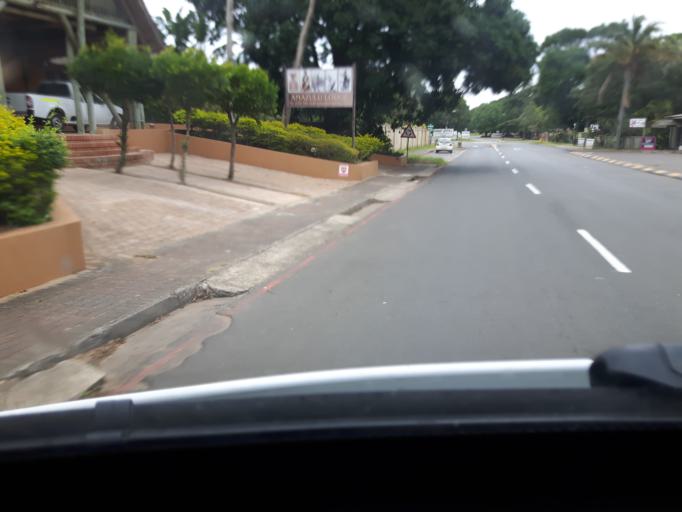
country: ZA
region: KwaZulu-Natal
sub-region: uMkhanyakude District Municipality
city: Mtubatuba
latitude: -28.3793
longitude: 32.4100
